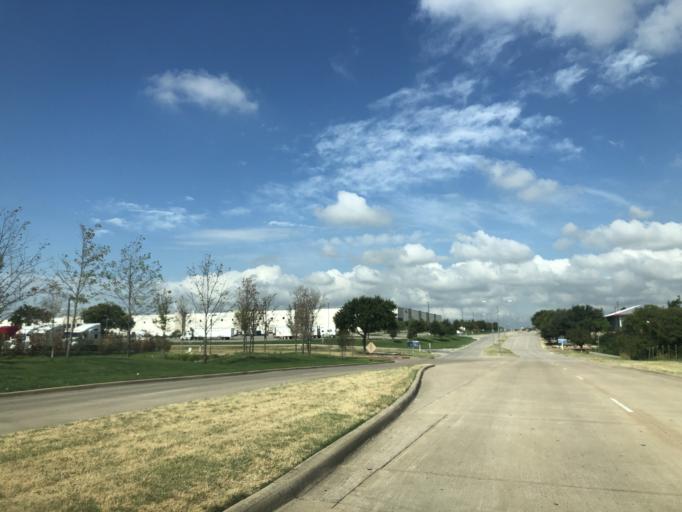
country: US
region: Texas
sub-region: Tarrant County
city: Haslet
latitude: 32.9740
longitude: -97.3311
